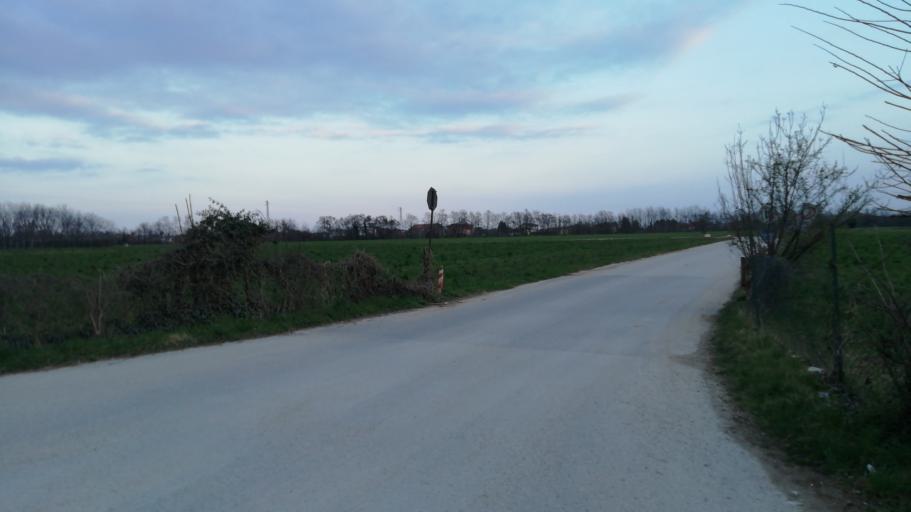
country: IT
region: Veneto
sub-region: Provincia di Vicenza
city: Marano Vicentino
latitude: 45.7003
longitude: 11.4520
